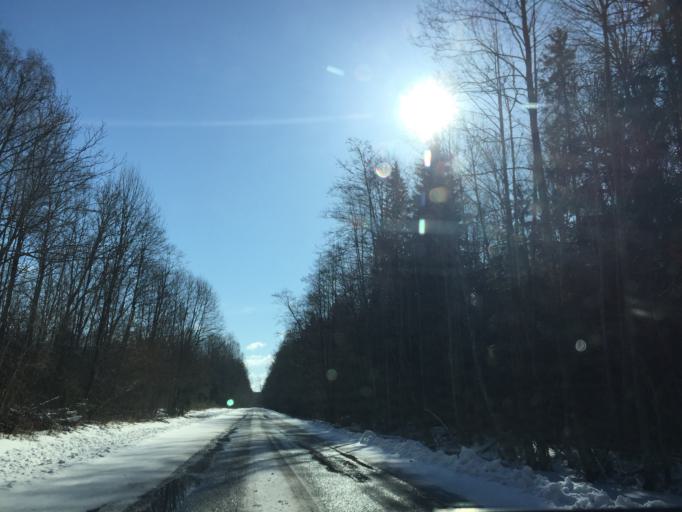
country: LV
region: Salacgrivas
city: Ainazi
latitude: 58.0011
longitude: 24.5220
